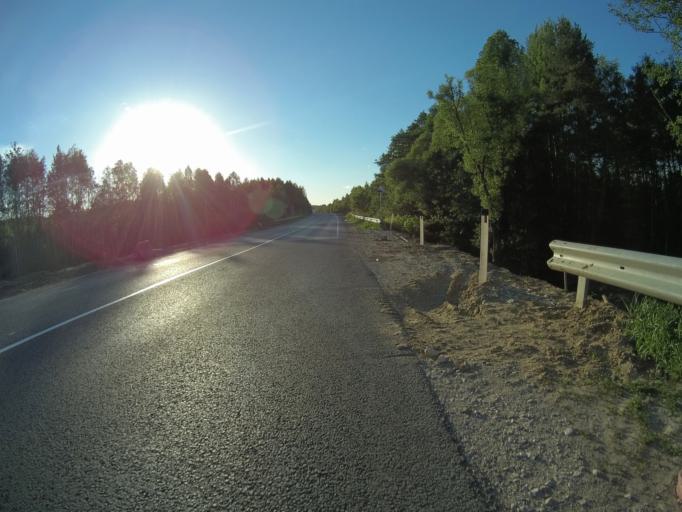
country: RU
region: Vladimir
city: Golovino
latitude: 55.9466
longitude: 40.5816
